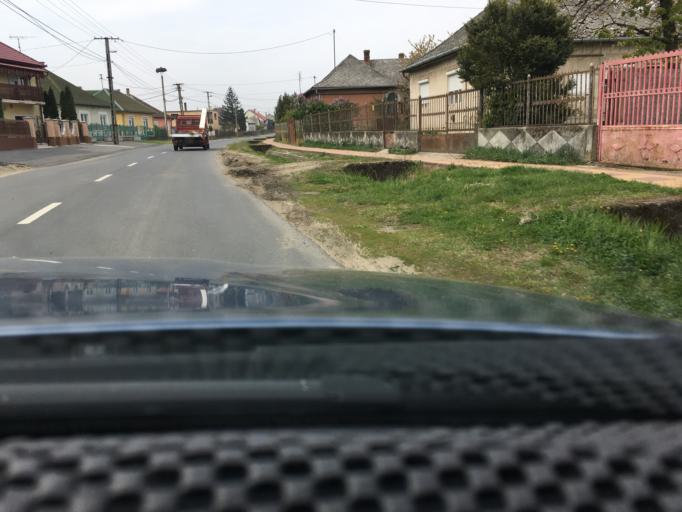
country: HU
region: Szabolcs-Szatmar-Bereg
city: Nyirbeltek
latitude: 47.6969
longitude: 22.1256
